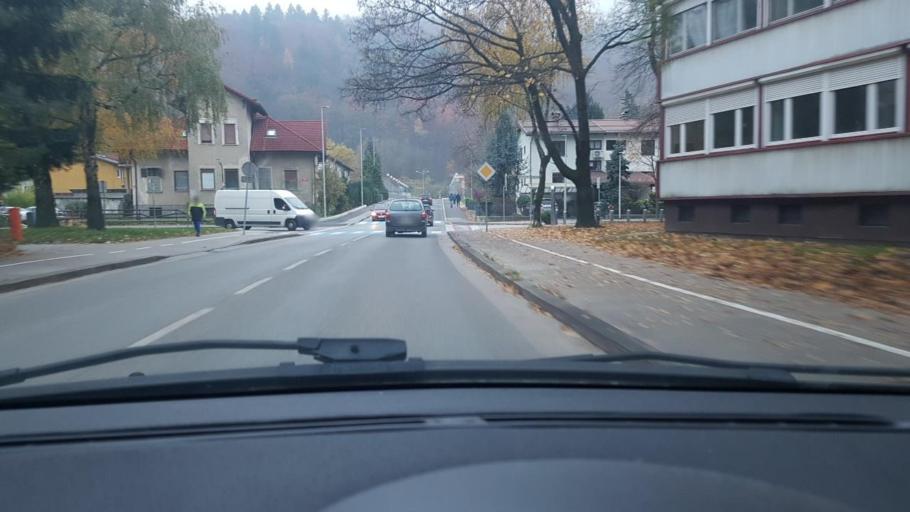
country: SI
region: Celje
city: Celje
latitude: 46.2333
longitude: 15.2530
